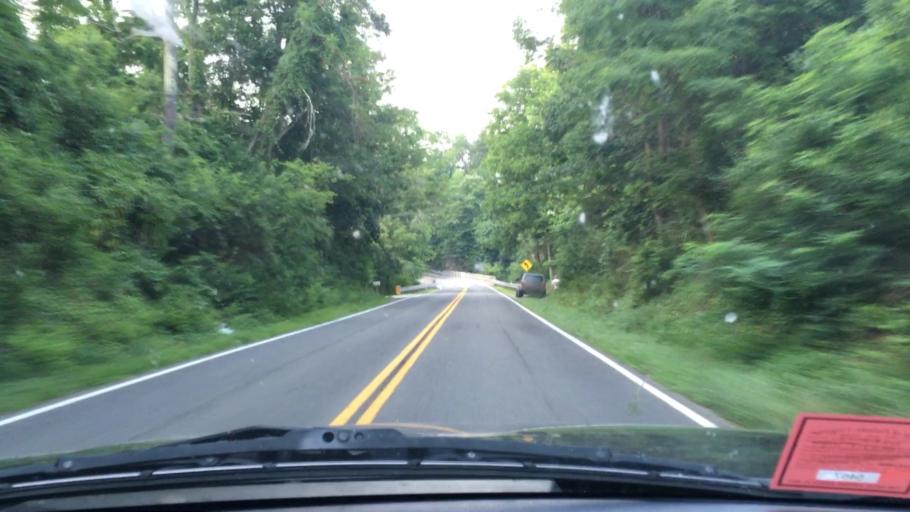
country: US
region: Virginia
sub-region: Pulaski County
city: Pulaski
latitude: 37.0443
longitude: -80.7132
